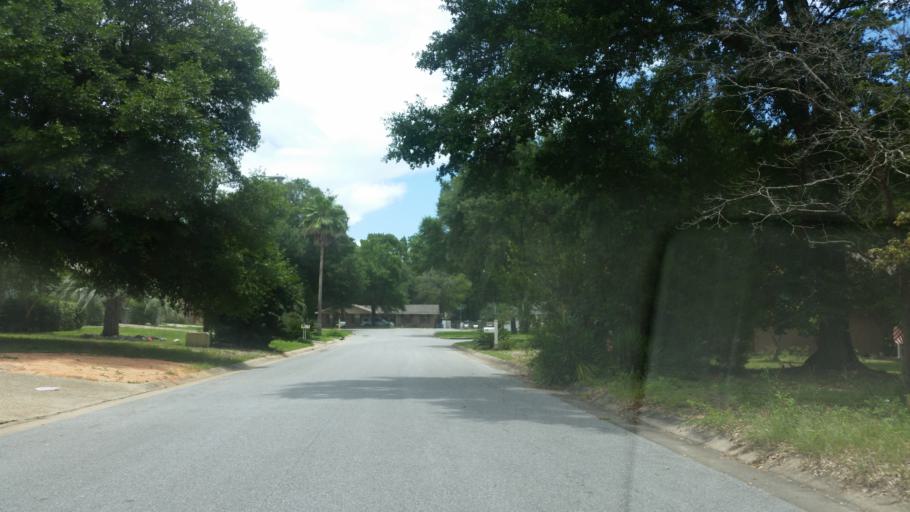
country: US
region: Florida
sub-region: Escambia County
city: Ferry Pass
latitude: 30.5158
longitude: -87.1866
